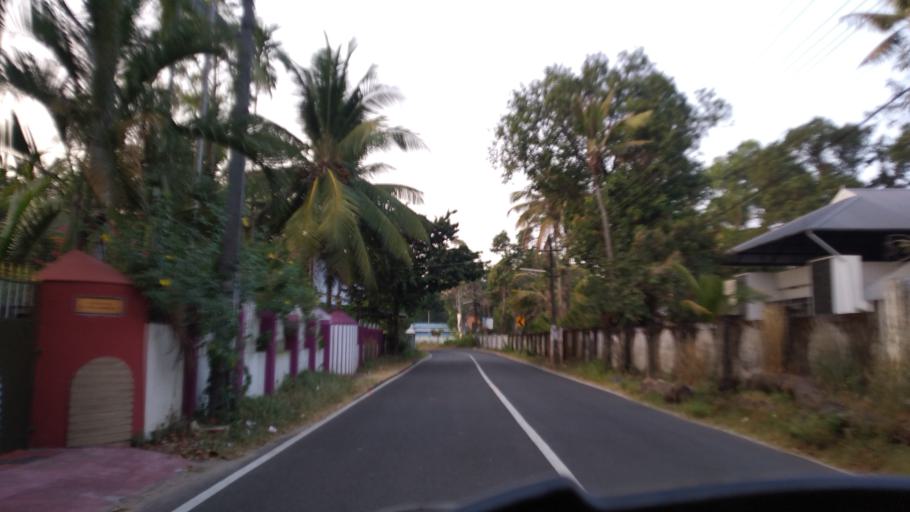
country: IN
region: Kerala
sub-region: Ernakulam
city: Elur
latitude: 10.1178
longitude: 76.2412
